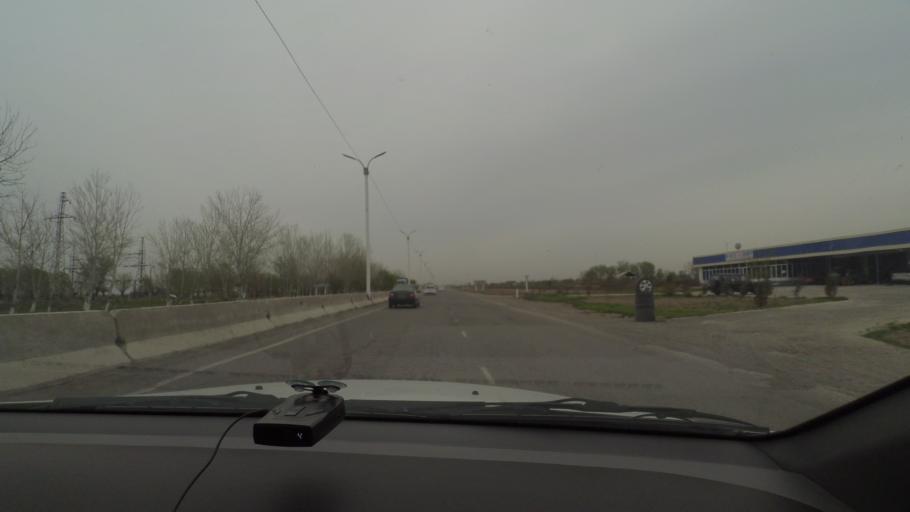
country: KZ
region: Ongtustik Qazaqstan
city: Myrzakent
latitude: 40.5388
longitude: 68.4239
